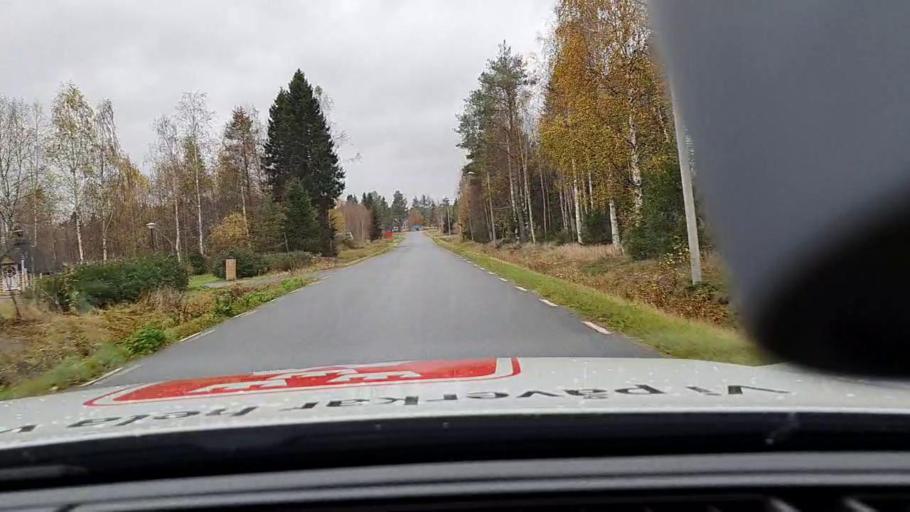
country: SE
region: Norrbotten
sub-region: Haparanda Kommun
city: Haparanda
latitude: 65.9455
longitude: 23.7994
